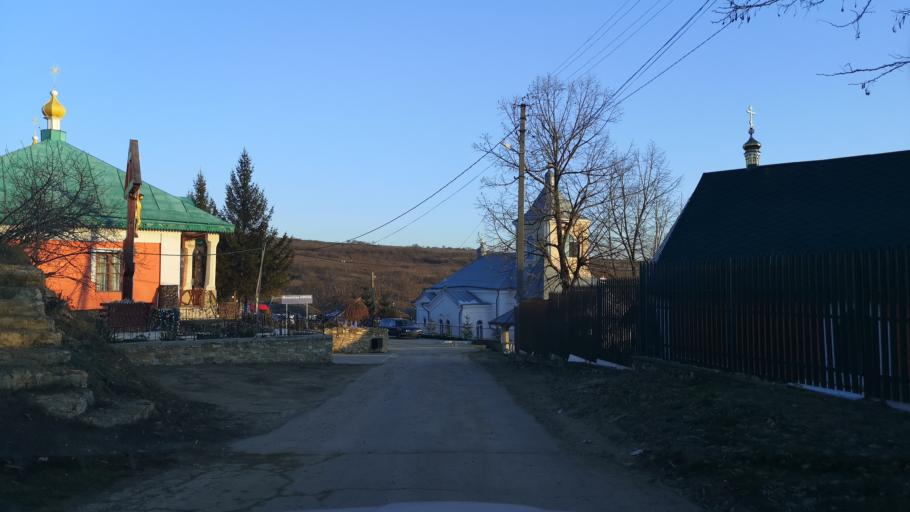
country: MD
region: Orhei
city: Orhei
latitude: 47.3683
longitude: 28.6908
